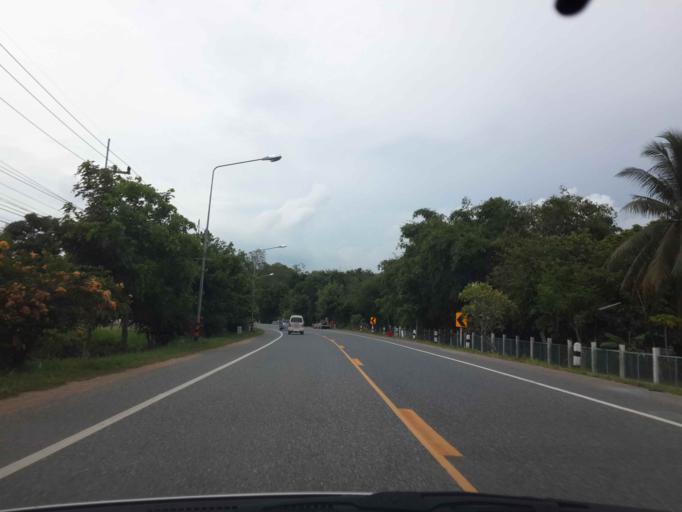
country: TH
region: Chon Buri
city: Si Racha
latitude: 13.2321
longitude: 100.9802
